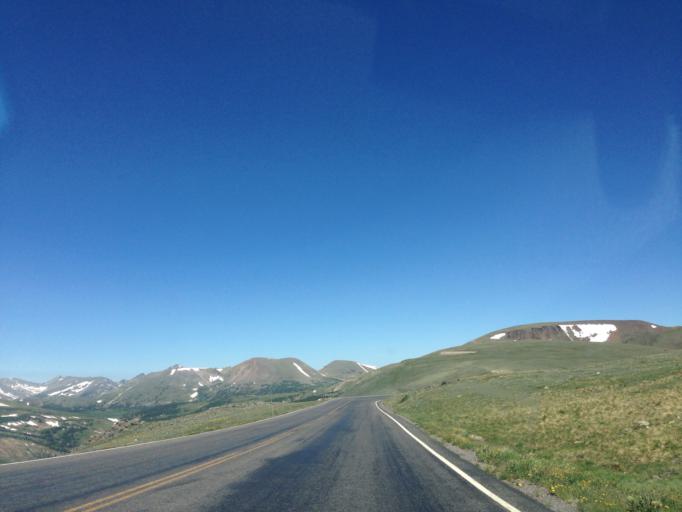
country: US
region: Colorado
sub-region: Larimer County
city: Estes Park
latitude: 40.4125
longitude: -105.7436
